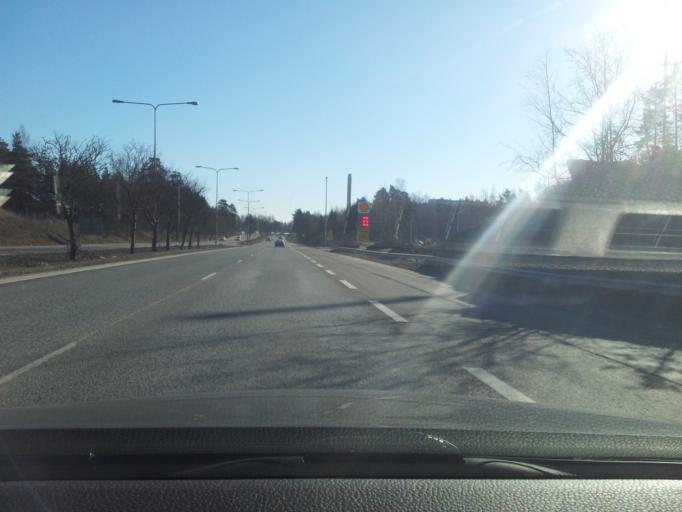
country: FI
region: Uusimaa
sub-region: Helsinki
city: Vantaa
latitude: 60.2287
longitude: 25.0633
